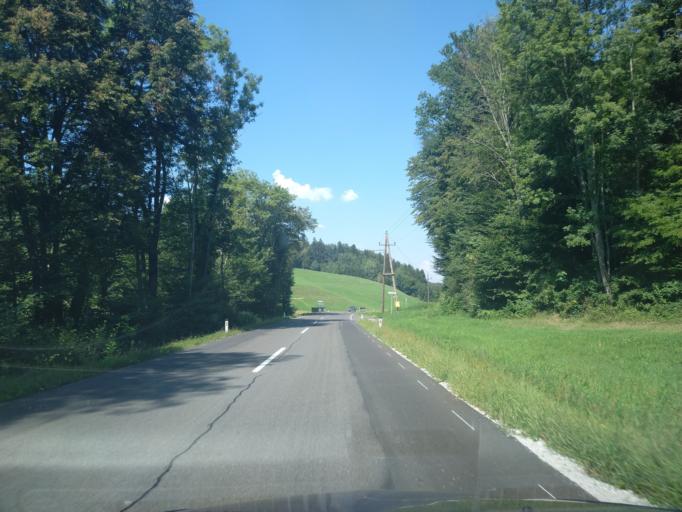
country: AT
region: Styria
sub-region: Politischer Bezirk Leibnitz
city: Sulztal an der Weinstrasse
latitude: 46.7042
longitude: 15.5039
